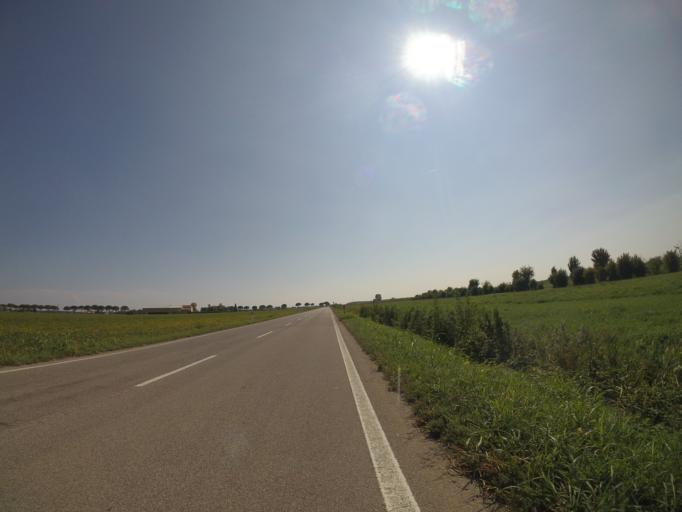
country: IT
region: Friuli Venezia Giulia
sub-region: Provincia di Udine
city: Carlino
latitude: 45.7912
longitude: 13.1652
